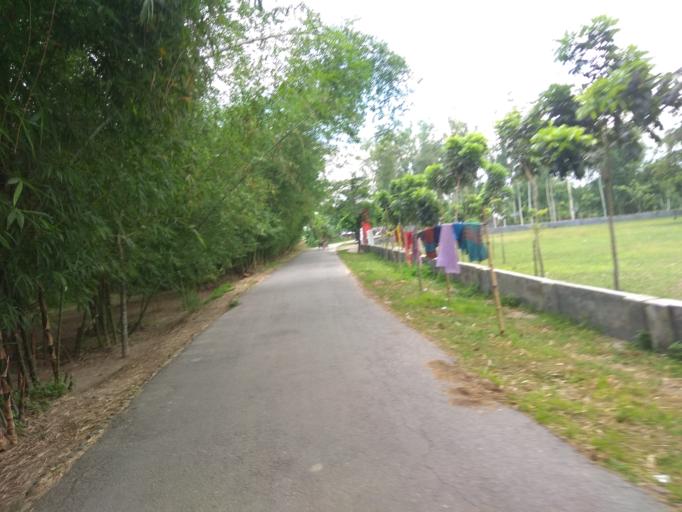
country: IN
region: West Bengal
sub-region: Koch Bihar
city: Haldibari
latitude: 26.1992
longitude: 88.9222
